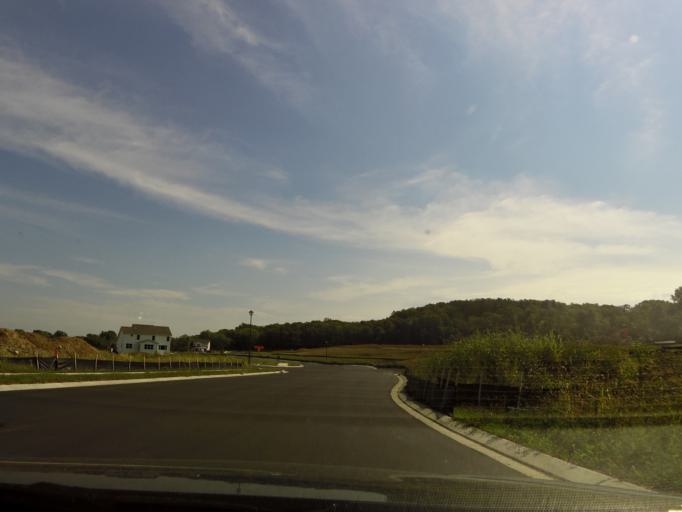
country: US
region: Minnesota
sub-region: Scott County
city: Prior Lake
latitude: 44.7629
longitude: -93.4193
